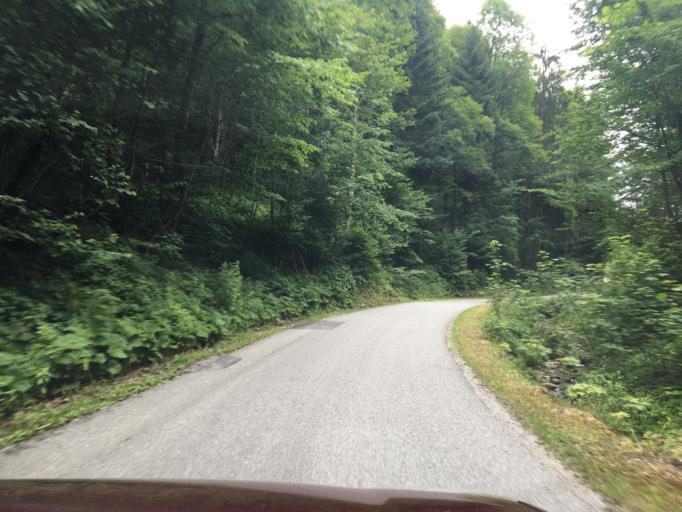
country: AT
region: Salzburg
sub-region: Politischer Bezirk Hallein
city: Scheffau am Tennengebirge
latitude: 47.6216
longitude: 13.2183
